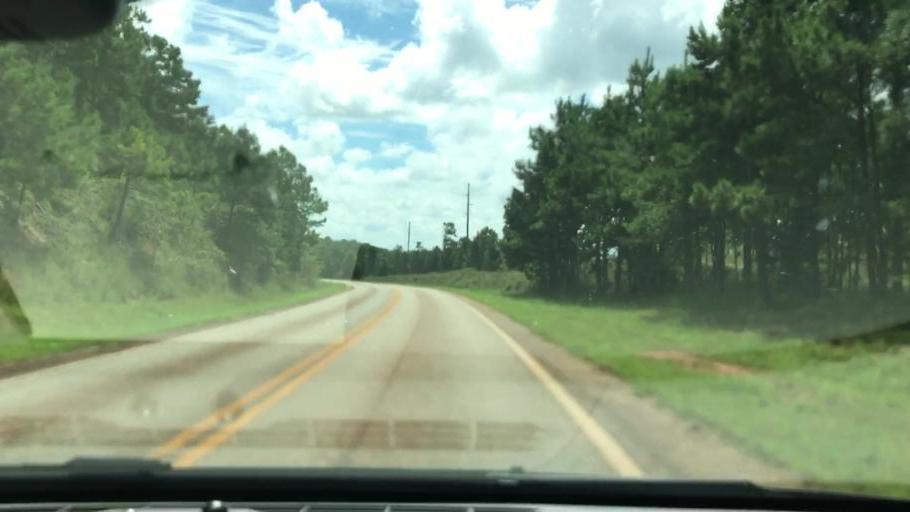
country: US
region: Georgia
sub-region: Stewart County
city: Lumpkin
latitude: 32.0651
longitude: -84.8383
